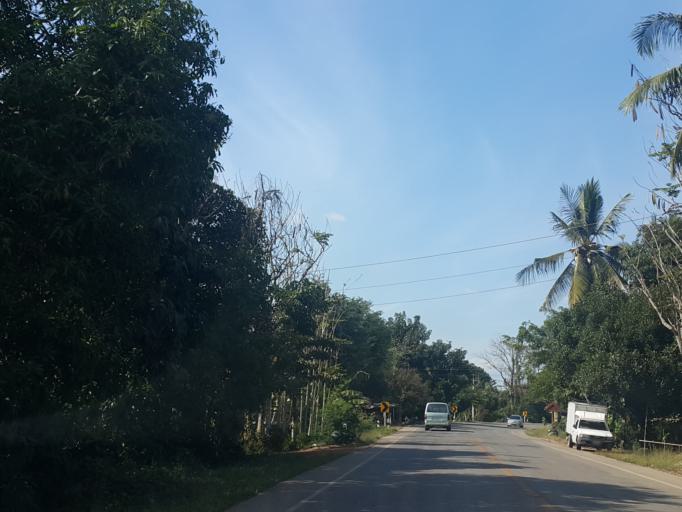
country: TH
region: Sukhothai
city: Sawankhalok
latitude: 17.2680
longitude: 99.8325
